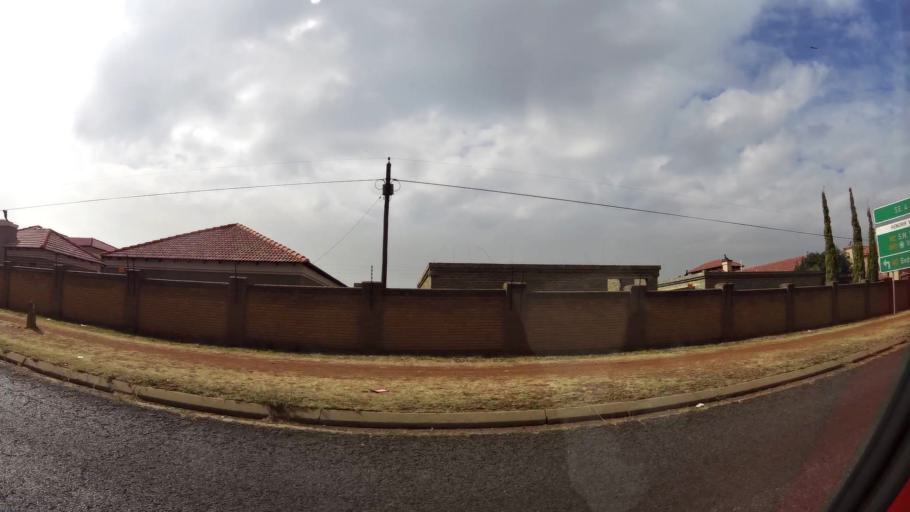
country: ZA
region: Gauteng
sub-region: Sedibeng District Municipality
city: Vanderbijlpark
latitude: -26.7273
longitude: 27.8629
